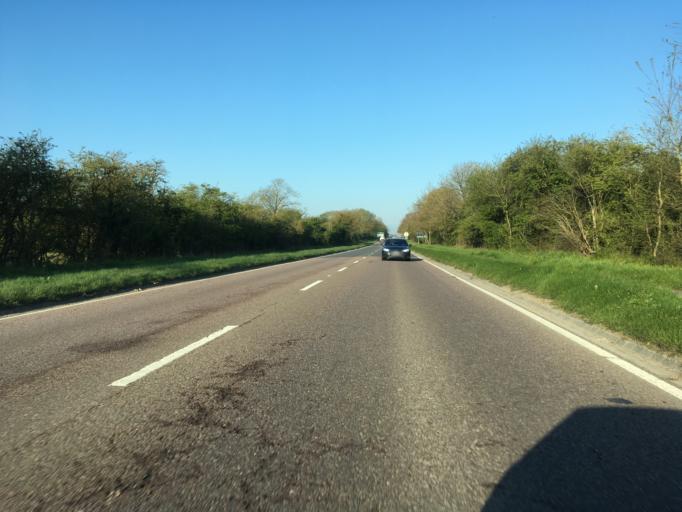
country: GB
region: England
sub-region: Oxfordshire
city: Yarnton
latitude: 51.7908
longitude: -1.3384
